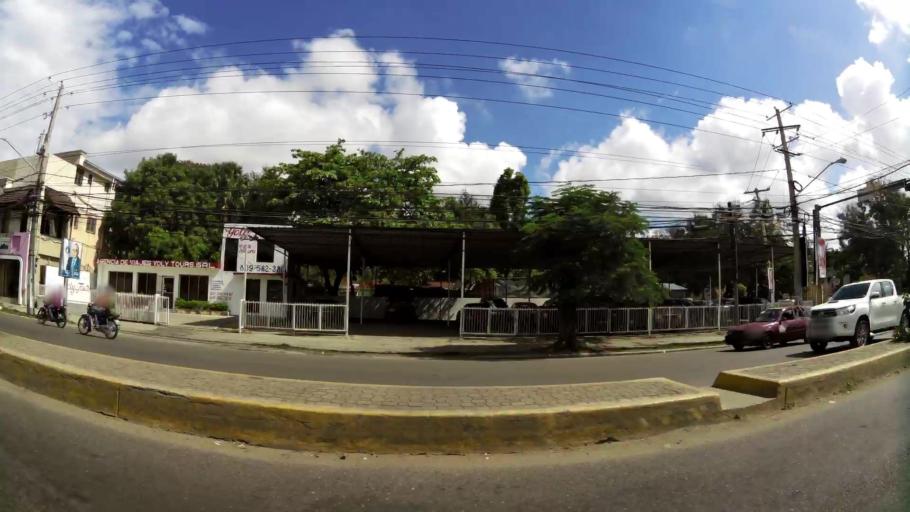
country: DO
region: Santiago
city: Santiago de los Caballeros
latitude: 19.4699
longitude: -70.6882
